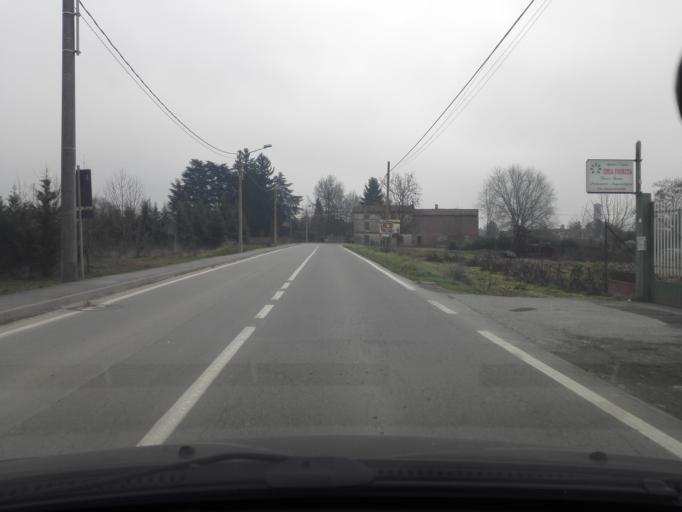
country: IT
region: Piedmont
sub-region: Provincia di Alessandria
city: Casal Cermelli
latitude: 44.8402
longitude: 8.6217
